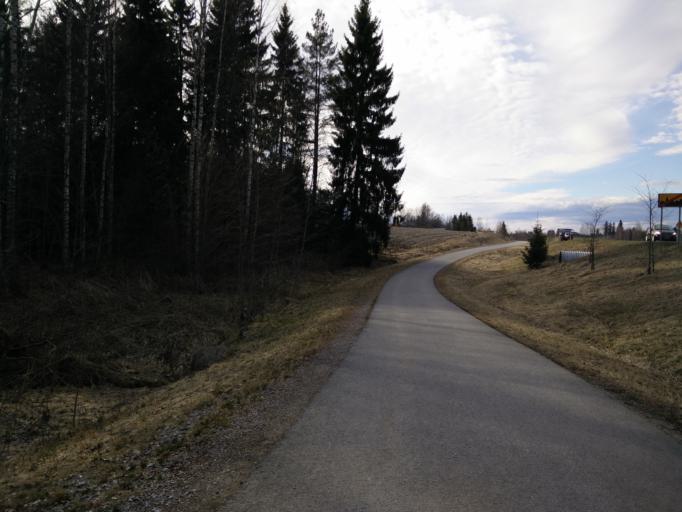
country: FI
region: Pirkanmaa
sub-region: Tampere
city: Orivesi
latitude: 61.6967
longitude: 24.3471
